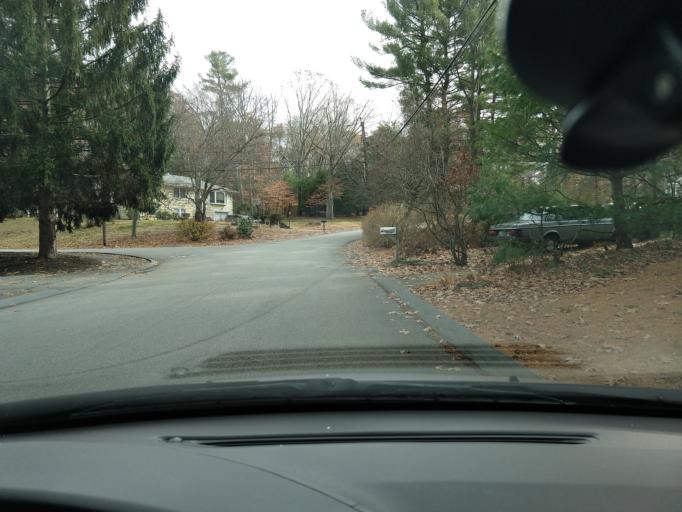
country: US
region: Massachusetts
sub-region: Middlesex County
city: Bedford
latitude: 42.4949
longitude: -71.2480
